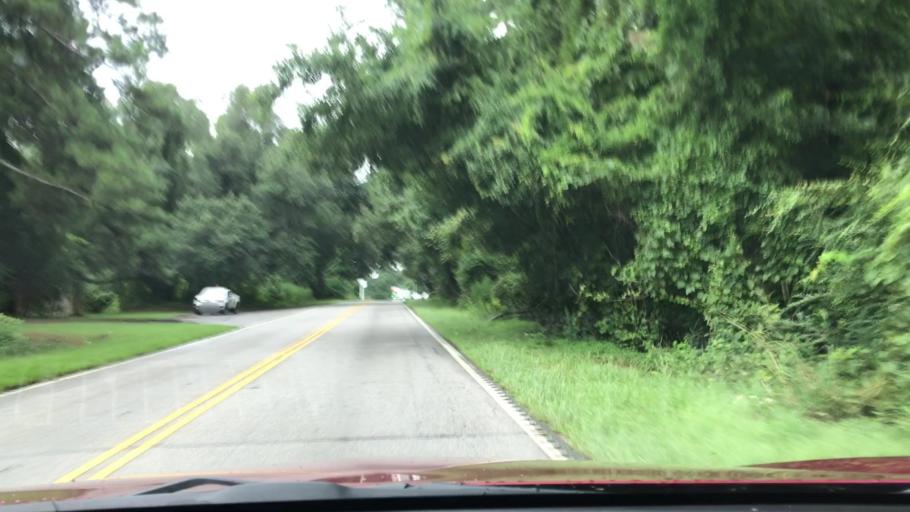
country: US
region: South Carolina
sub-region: Georgetown County
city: Murrells Inlet
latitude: 33.5574
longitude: -79.2157
